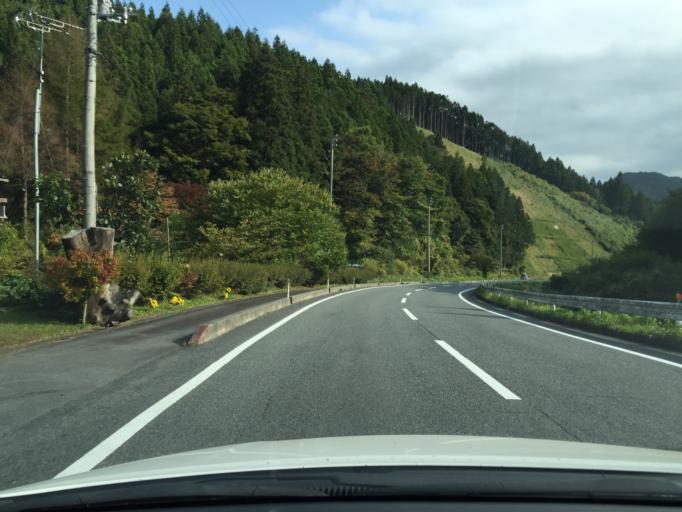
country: JP
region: Ibaraki
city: Kitaibaraki
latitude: 36.9558
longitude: 140.6244
